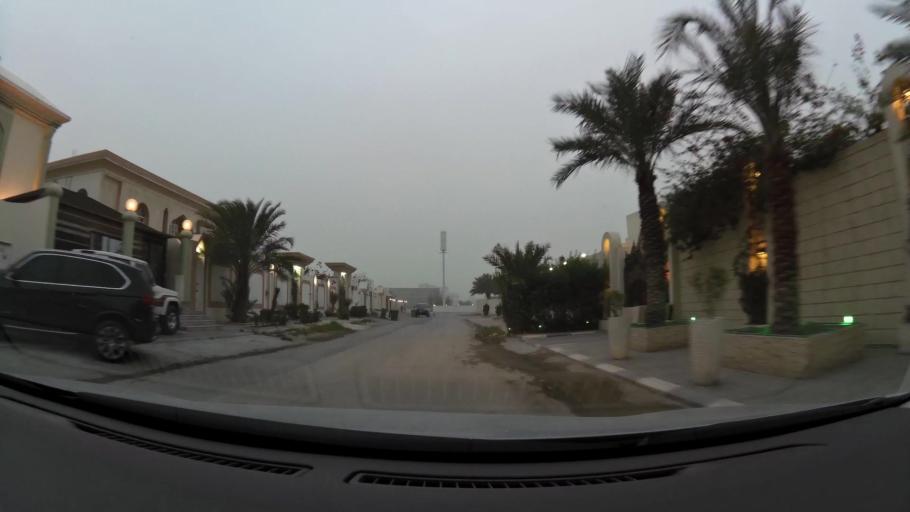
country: QA
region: Baladiyat ad Dawhah
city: Doha
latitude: 25.2279
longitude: 51.4960
